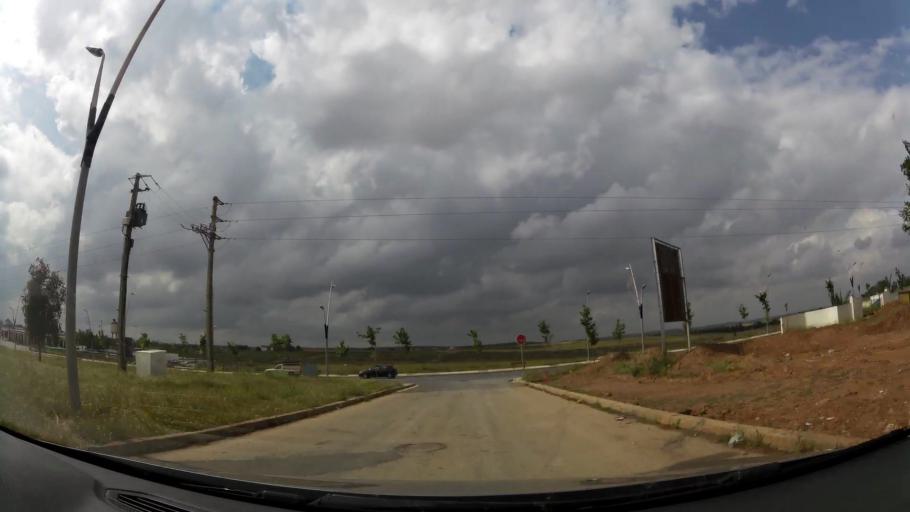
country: MA
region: Rabat-Sale-Zemmour-Zaer
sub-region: Khemisset
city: Tiflet
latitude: 33.8957
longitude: -6.3420
